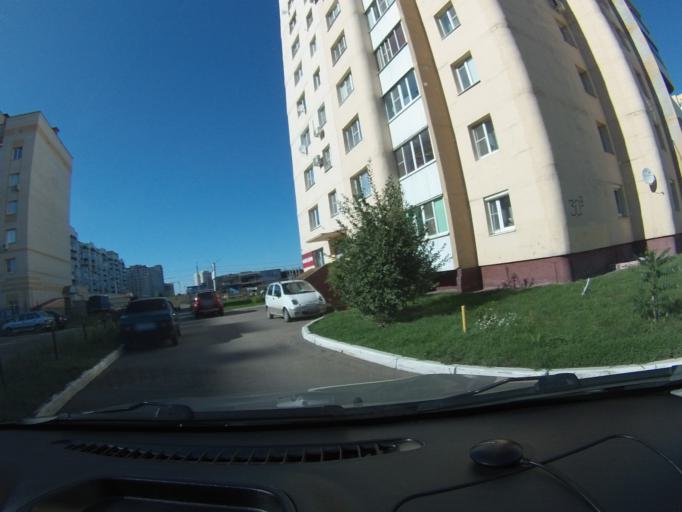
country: RU
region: Tambov
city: Tambov
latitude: 52.7690
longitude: 41.4073
